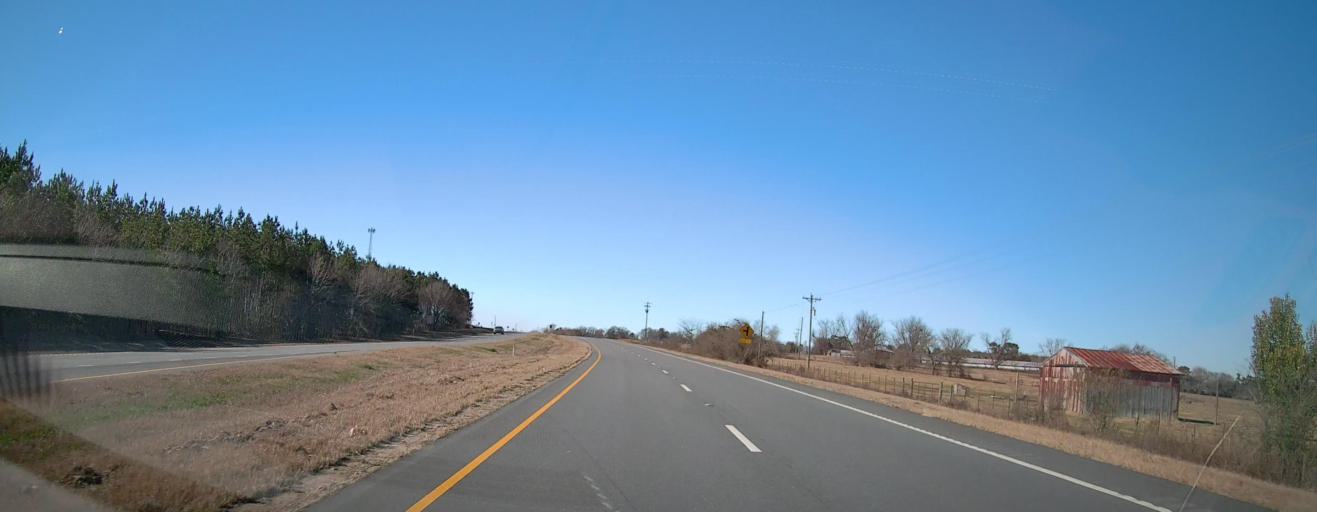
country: US
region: Georgia
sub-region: Taylor County
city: Butler
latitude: 32.6231
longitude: -84.2486
